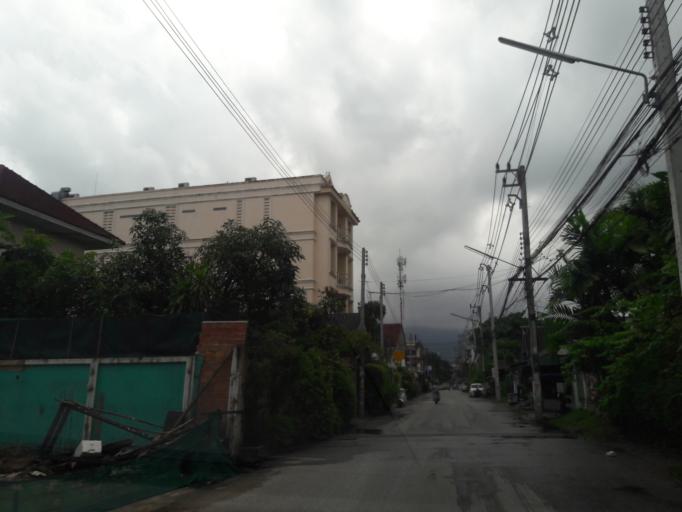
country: TH
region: Chiang Mai
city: Chiang Mai
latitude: 18.8054
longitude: 98.9763
